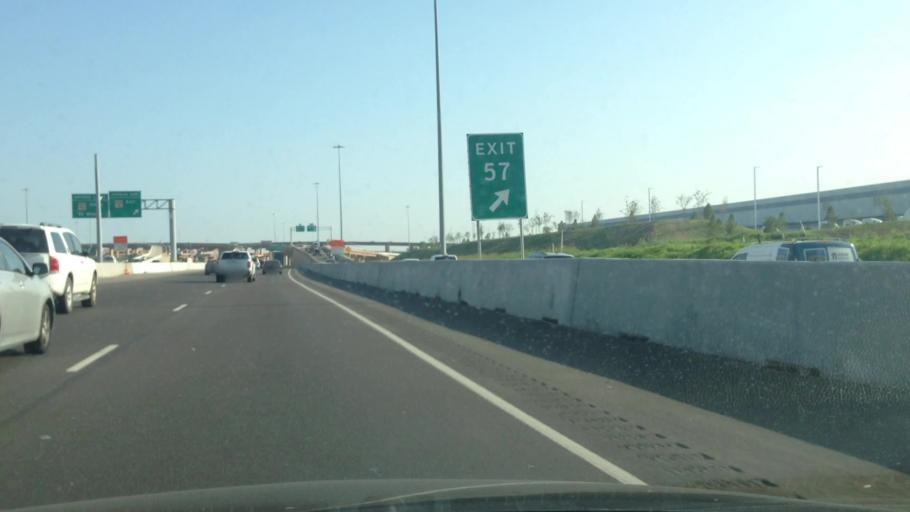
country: US
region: Texas
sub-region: Tarrant County
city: Blue Mound
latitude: 32.8481
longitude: -97.3131
